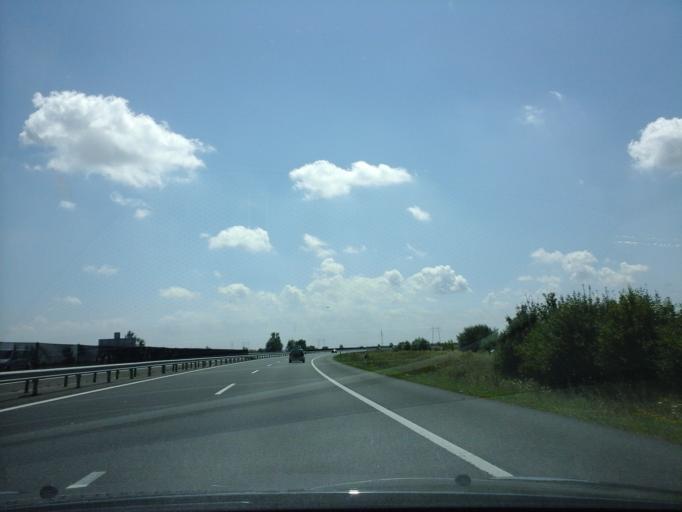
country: HU
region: Hajdu-Bihar
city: Polgar
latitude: 47.8423
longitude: 21.1506
